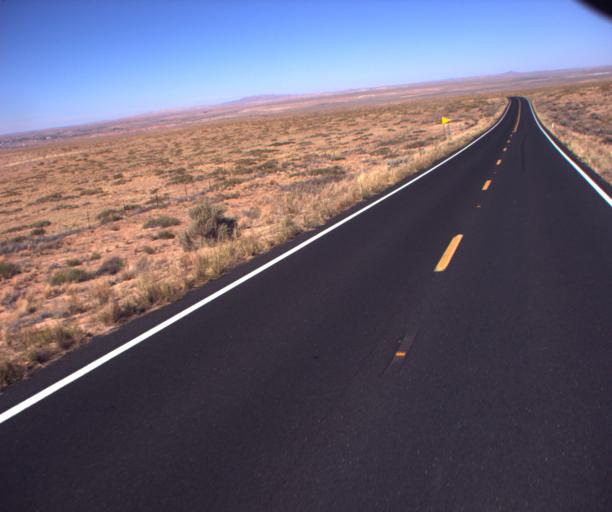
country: US
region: Arizona
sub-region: Coconino County
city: Tuba City
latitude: 36.0446
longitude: -111.1831
